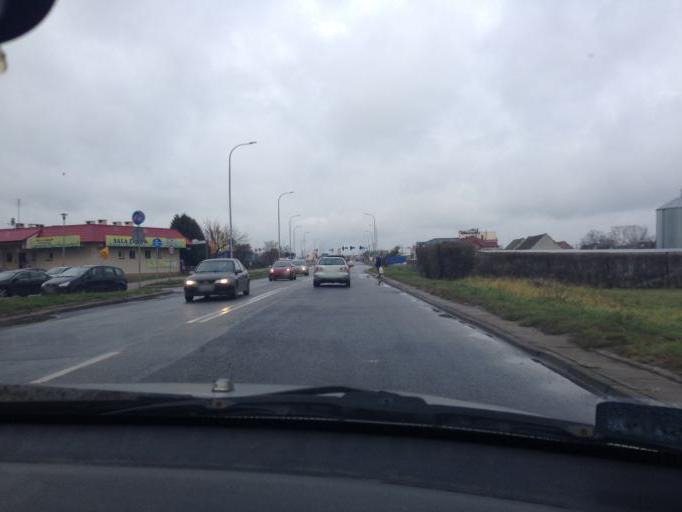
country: PL
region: Opole Voivodeship
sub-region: Powiat opolski
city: Opole
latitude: 50.6851
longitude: 17.9528
